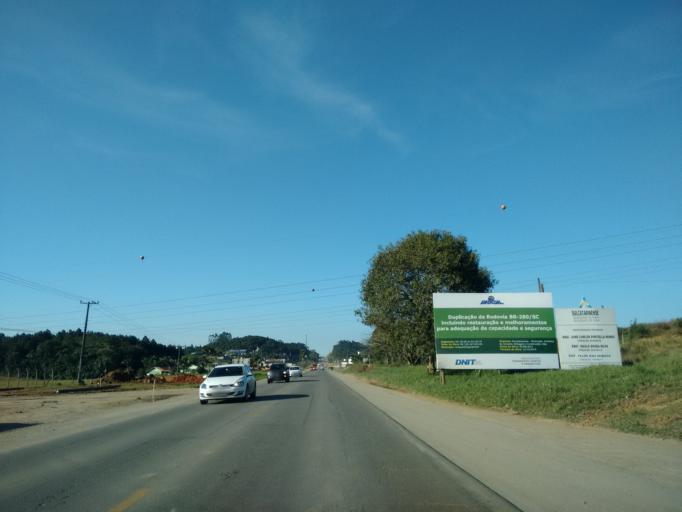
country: BR
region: Santa Catarina
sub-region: Guaramirim
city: Guaramirim
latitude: -26.4635
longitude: -48.9502
